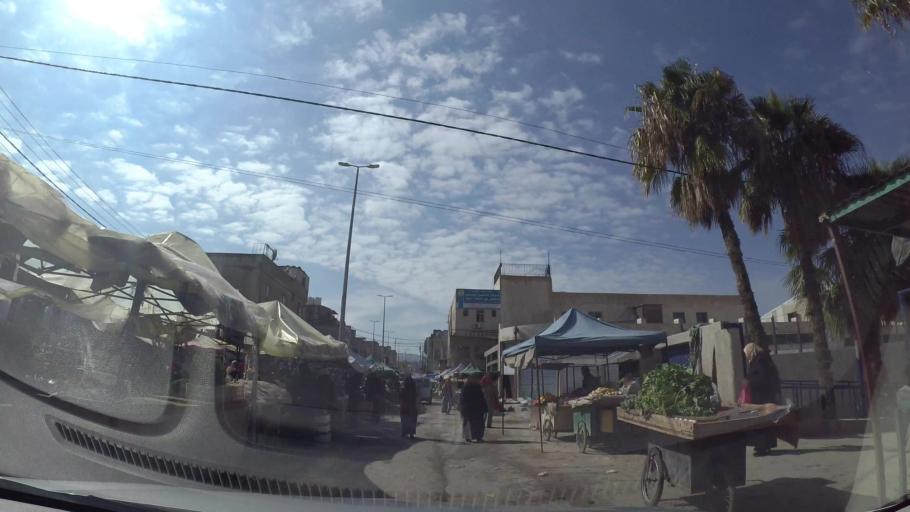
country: JO
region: Amman
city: Al Jubayhah
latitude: 32.0750
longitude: 35.8450
